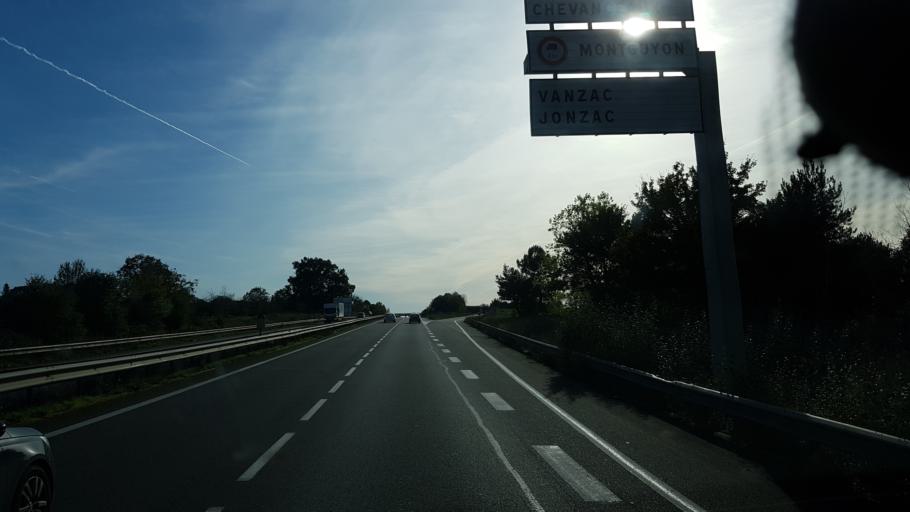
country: FR
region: Poitou-Charentes
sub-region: Departement de la Charente-Maritime
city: Chevanceaux
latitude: 45.3137
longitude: -0.2318
